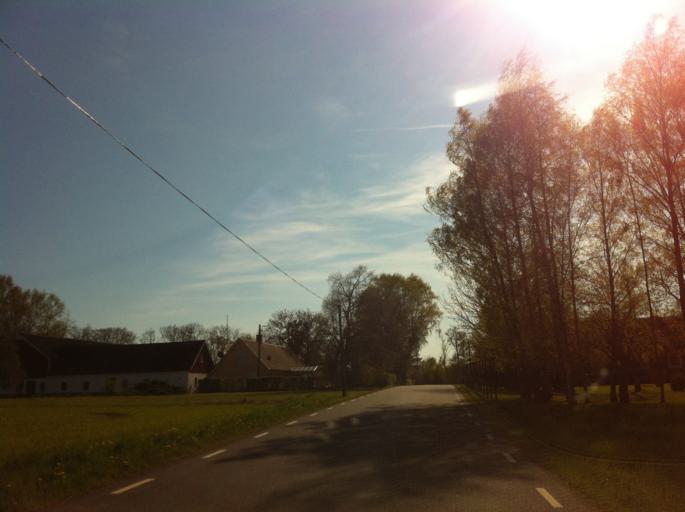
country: SE
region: Skane
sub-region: Svalovs Kommun
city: Kagerod
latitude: 55.9979
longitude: 13.0886
